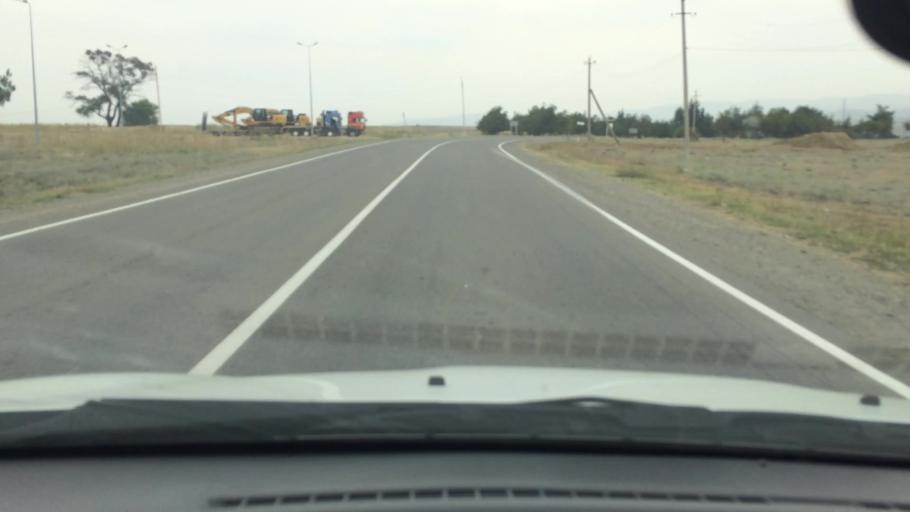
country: GE
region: Kvemo Kartli
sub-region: Gardabani
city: Gardabani
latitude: 41.3492
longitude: 45.0678
